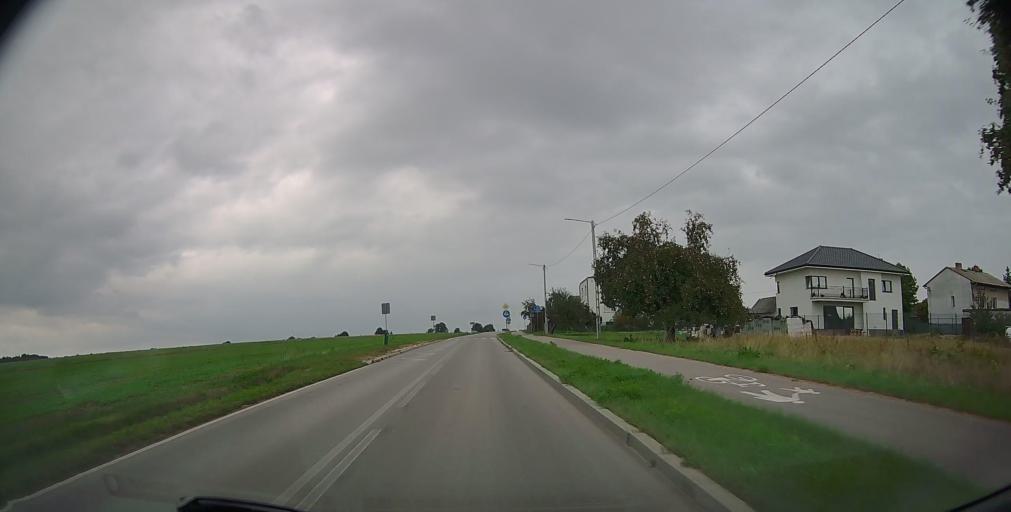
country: PL
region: Masovian Voivodeship
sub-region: Powiat radomski
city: Zakrzew
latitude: 51.4372
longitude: 21.0521
